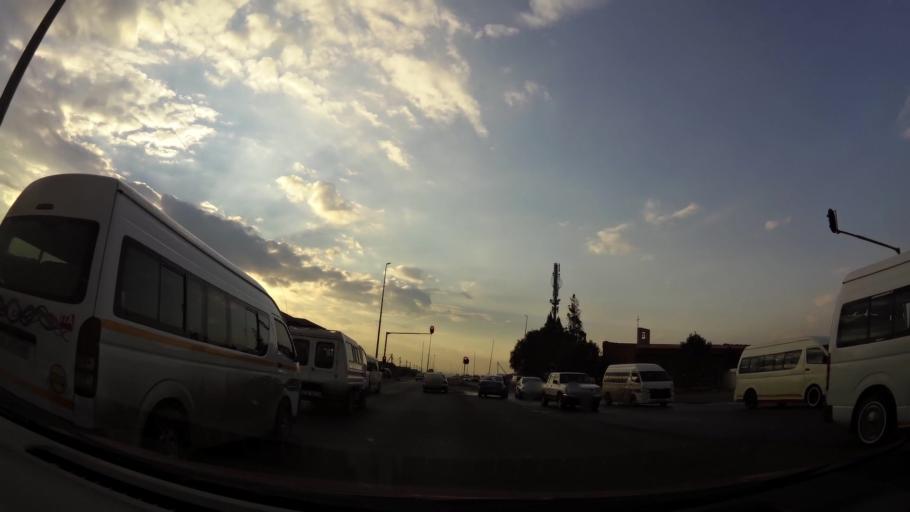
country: ZA
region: Gauteng
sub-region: City of Johannesburg Metropolitan Municipality
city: Orange Farm
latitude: -26.5728
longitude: 27.8385
